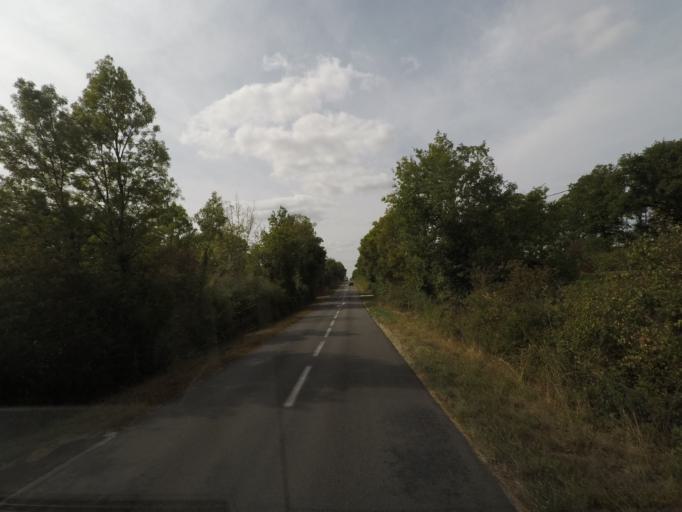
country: FR
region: Poitou-Charentes
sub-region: Departement de la Charente
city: Loubert
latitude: 45.9367
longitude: 0.5358
